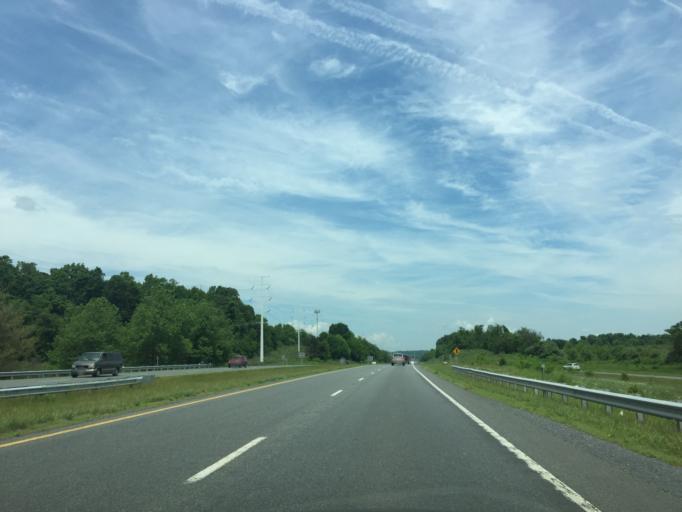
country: US
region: Virginia
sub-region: City of Winchester
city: Winchester
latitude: 39.1592
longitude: -78.2107
